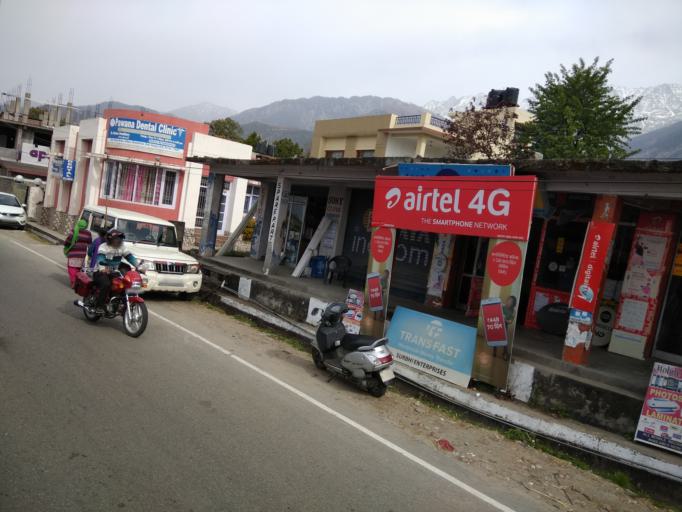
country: IN
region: Himachal Pradesh
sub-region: Kangra
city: Dharmsala
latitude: 32.1926
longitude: 76.3488
